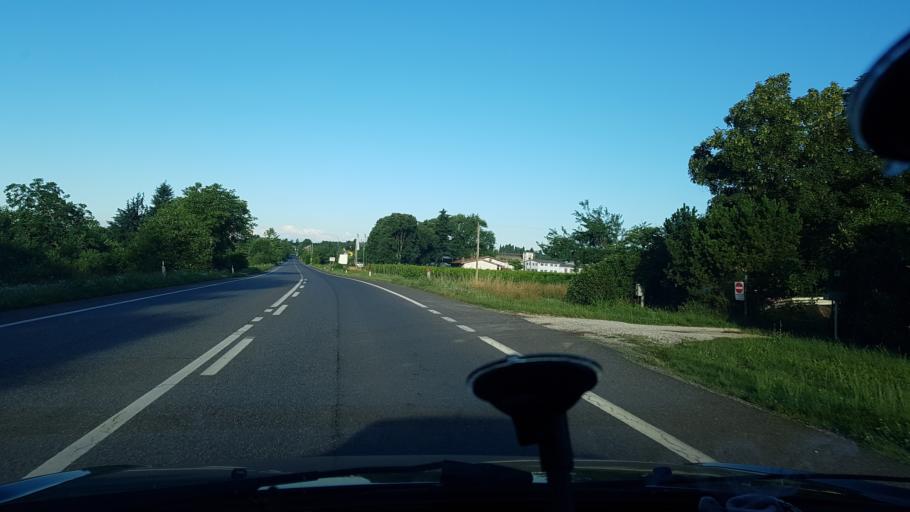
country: IT
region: Friuli Venezia Giulia
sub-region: Provincia di Gorizia
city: Savogna d'Isonzo
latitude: 45.9299
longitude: 13.5806
